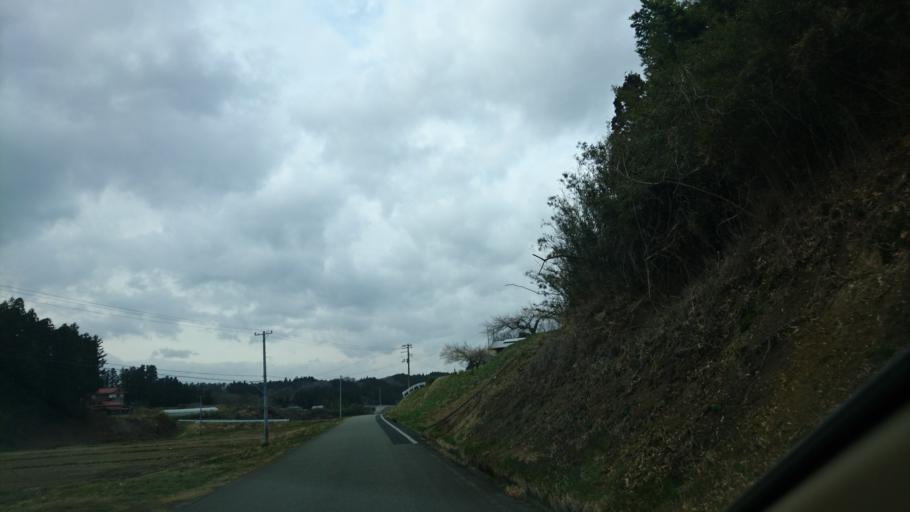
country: JP
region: Iwate
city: Ichinoseki
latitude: 38.8981
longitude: 141.1820
